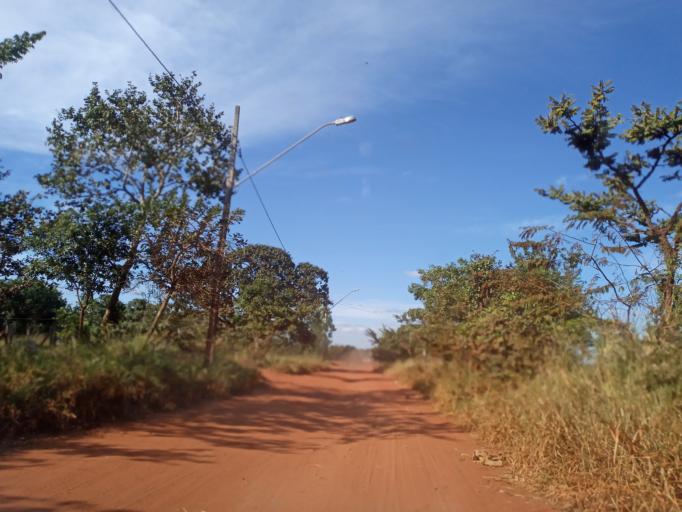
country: BR
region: Minas Gerais
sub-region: Ituiutaba
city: Ituiutaba
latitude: -18.9556
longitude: -49.4841
